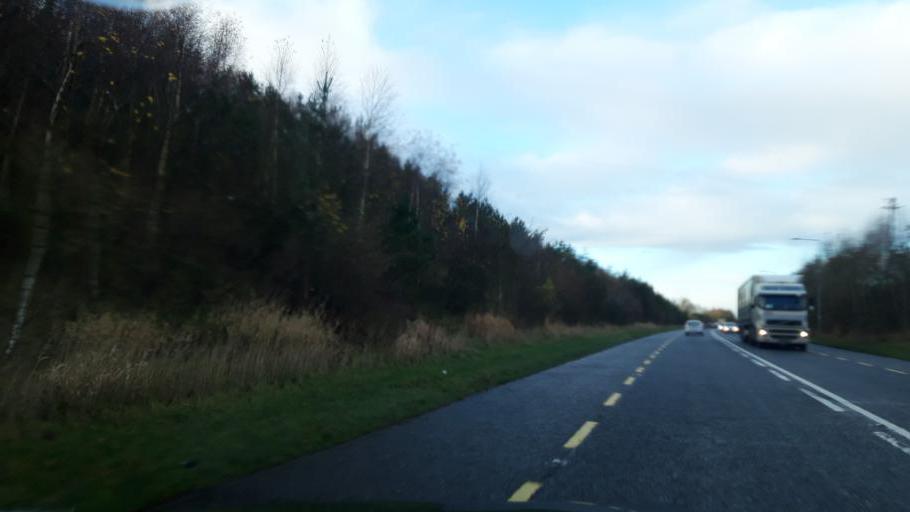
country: IE
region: Ulster
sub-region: County Monaghan
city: Carrickmacross
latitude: 53.9468
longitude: -6.6694
